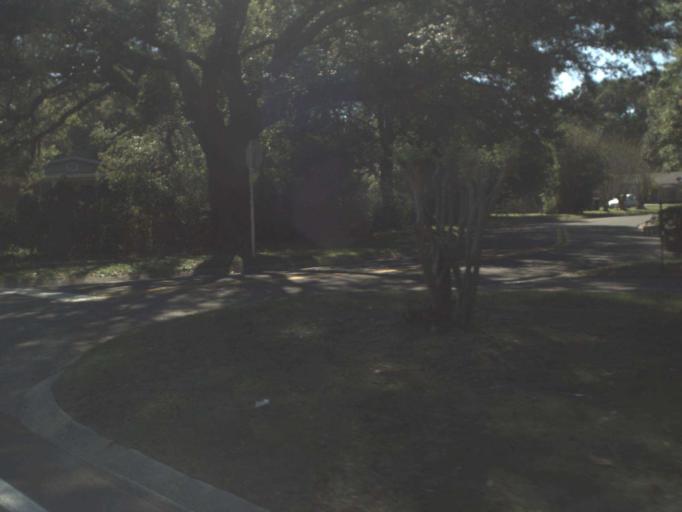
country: US
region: Florida
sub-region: Escambia County
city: Goulding
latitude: 30.4460
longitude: -87.2124
